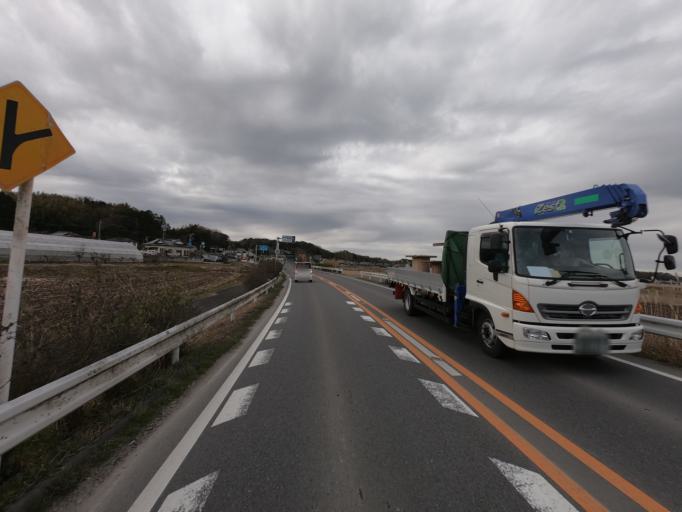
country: JP
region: Ibaraki
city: Ishioka
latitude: 36.0915
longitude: 140.3807
